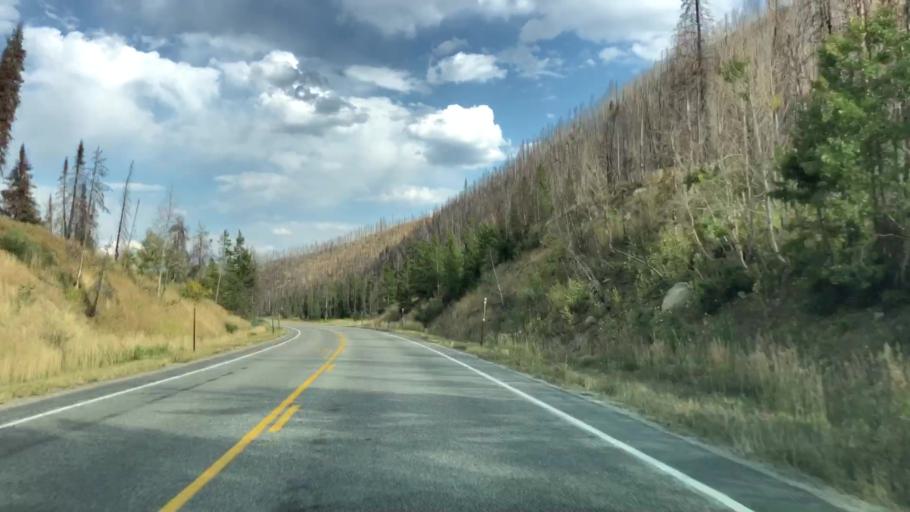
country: US
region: Wyoming
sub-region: Teton County
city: Hoback
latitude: 43.2450
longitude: -110.4891
